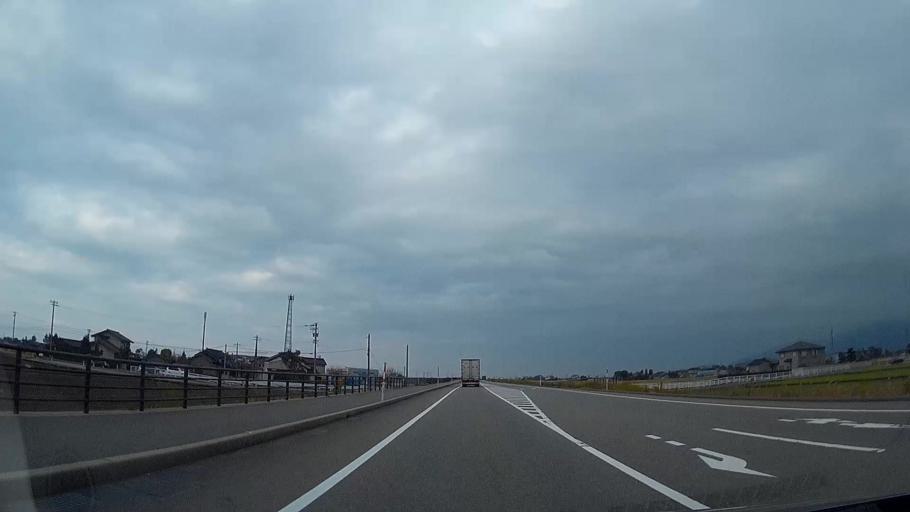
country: JP
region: Toyama
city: Nyuzen
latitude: 36.9217
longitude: 137.4679
